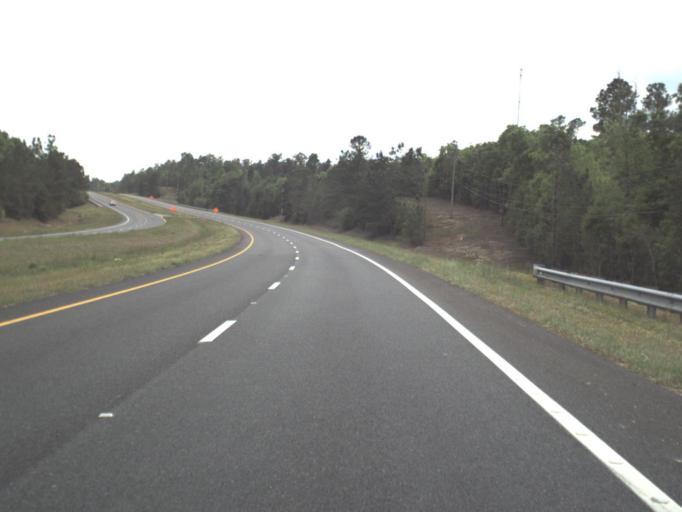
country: US
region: Florida
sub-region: Escambia County
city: Century
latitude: 30.8983
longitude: -87.3202
